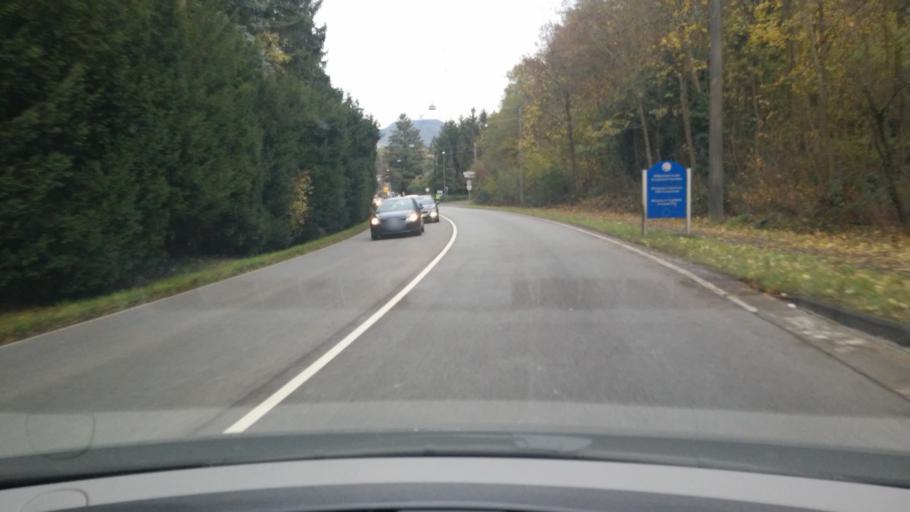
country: DE
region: Saarland
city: Saarlouis
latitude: 49.3018
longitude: 6.7331
